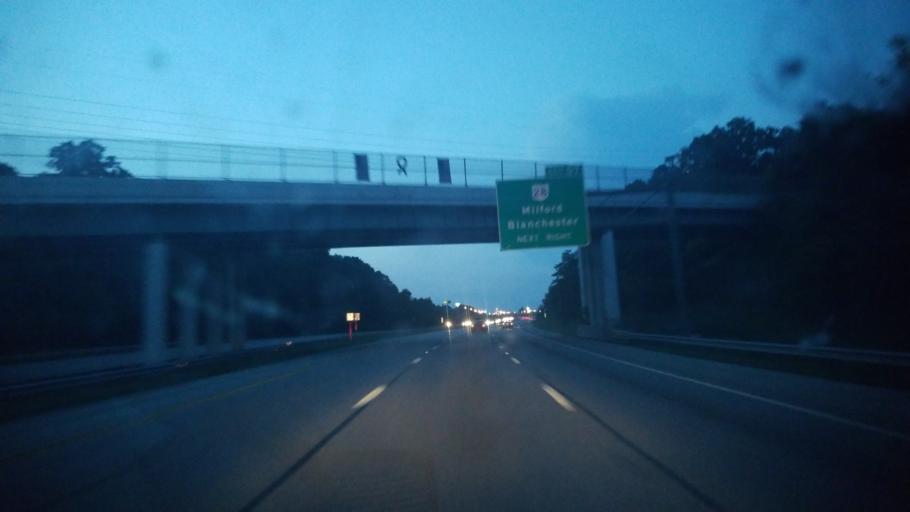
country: US
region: Ohio
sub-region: Clermont County
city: Milford
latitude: 39.1754
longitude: -84.2675
